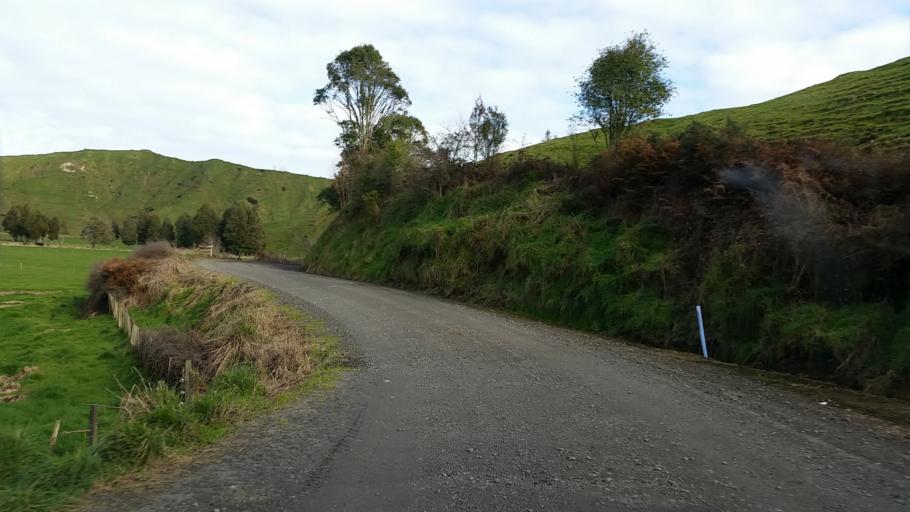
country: NZ
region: Taranaki
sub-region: South Taranaki District
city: Eltham
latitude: -39.2561
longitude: 174.5118
